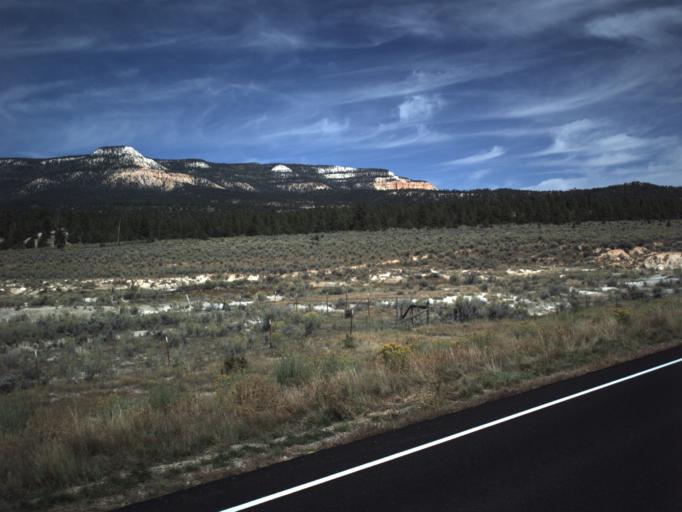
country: US
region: Utah
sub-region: Garfield County
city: Panguitch
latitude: 37.6712
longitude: -111.8291
